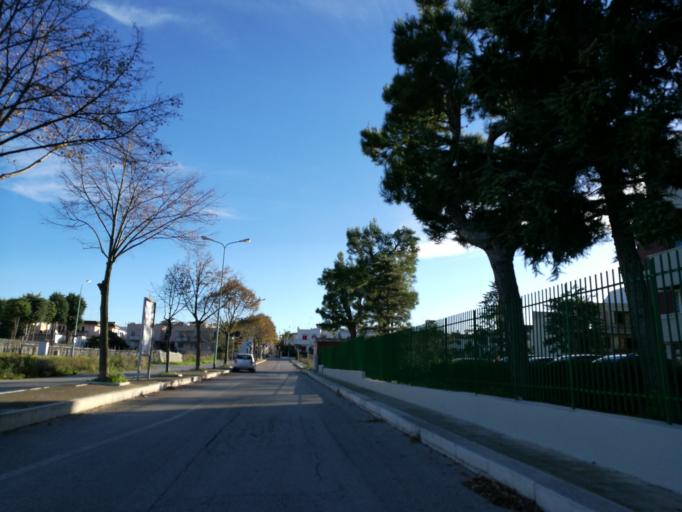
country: IT
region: Apulia
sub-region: Provincia di Bari
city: Adelfia
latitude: 41.0075
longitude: 16.8696
